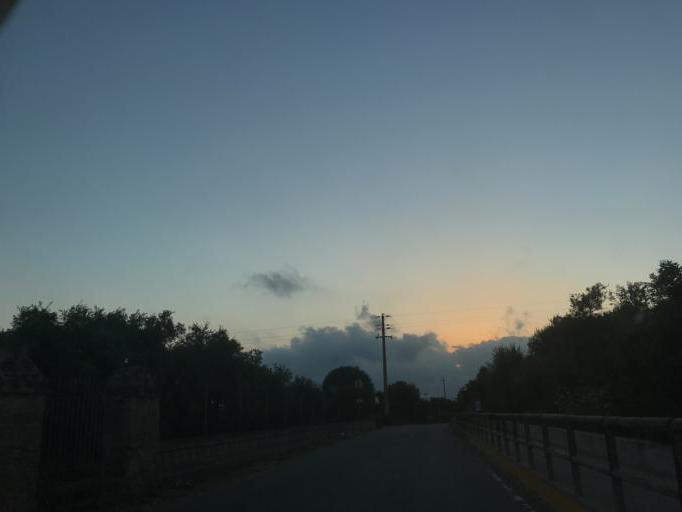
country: IT
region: Sardinia
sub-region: Provincia di Sassari
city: Alghero
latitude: 40.5520
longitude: 8.3403
